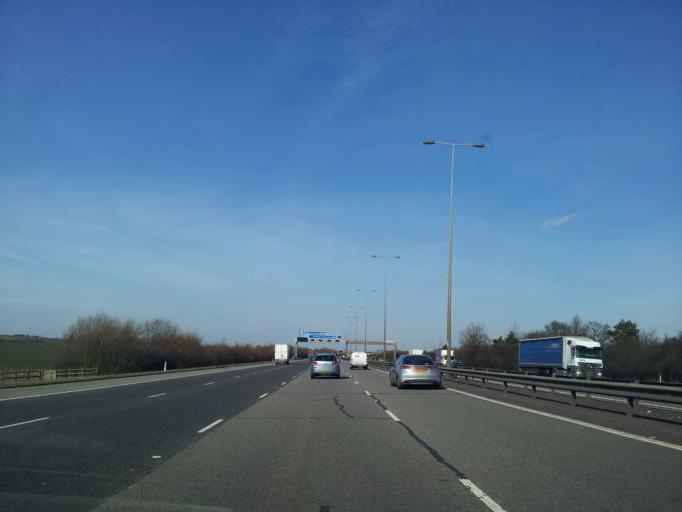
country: GB
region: England
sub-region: Cambridgeshire
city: Sawtry
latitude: 52.4150
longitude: -0.2668
